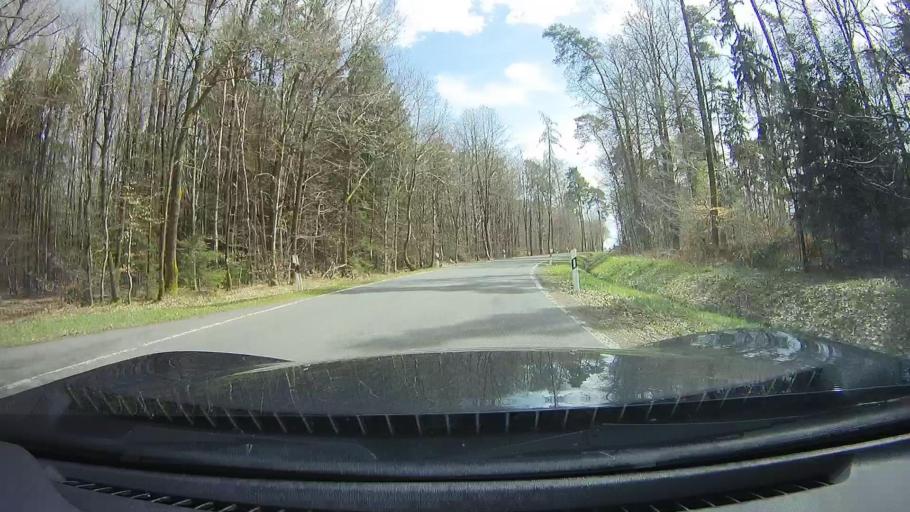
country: DE
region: Hesse
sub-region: Regierungsbezirk Darmstadt
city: Hesseneck
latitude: 49.6268
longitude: 9.1054
